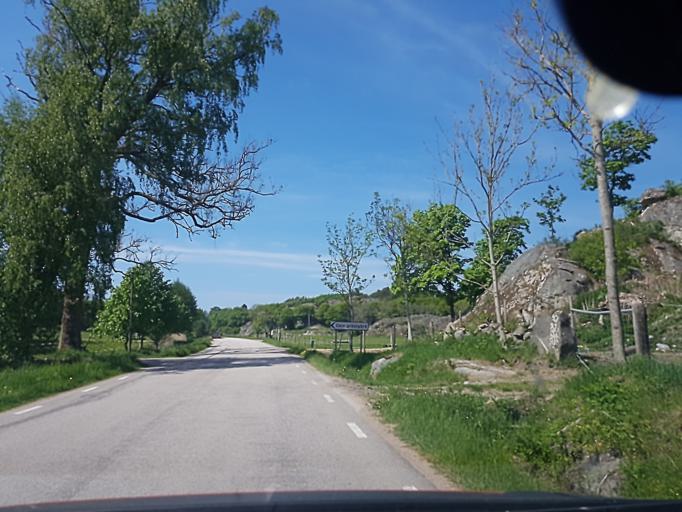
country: SE
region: Vaestra Goetaland
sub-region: Lysekils Kommun
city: Lysekil
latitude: 58.1611
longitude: 11.4553
